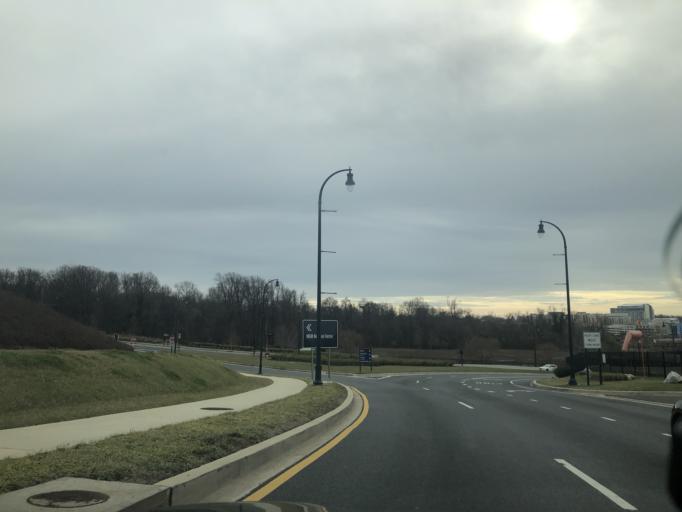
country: US
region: Maryland
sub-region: Prince George's County
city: Forest Heights
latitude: 38.7942
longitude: -77.0117
